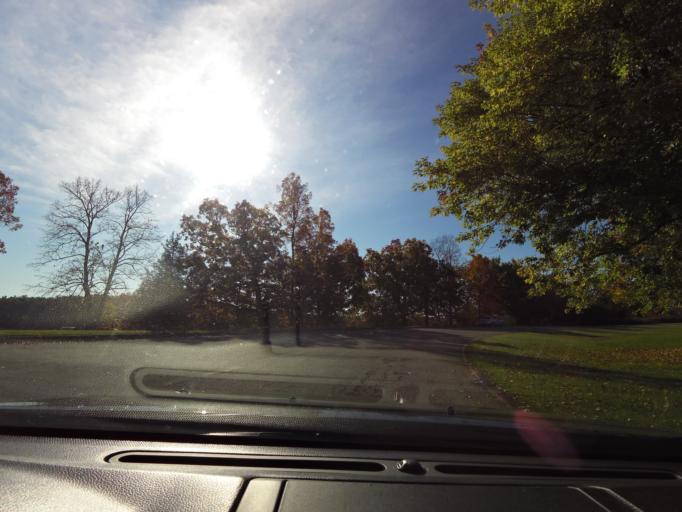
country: US
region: New York
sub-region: Livingston County
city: Mount Morris
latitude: 42.7322
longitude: -77.9154
